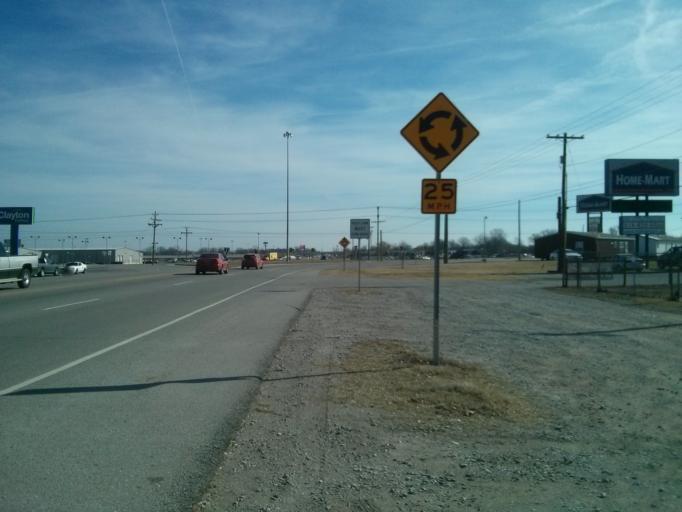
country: US
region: Oklahoma
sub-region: Tulsa County
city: Owasso
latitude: 36.1606
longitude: -95.8705
